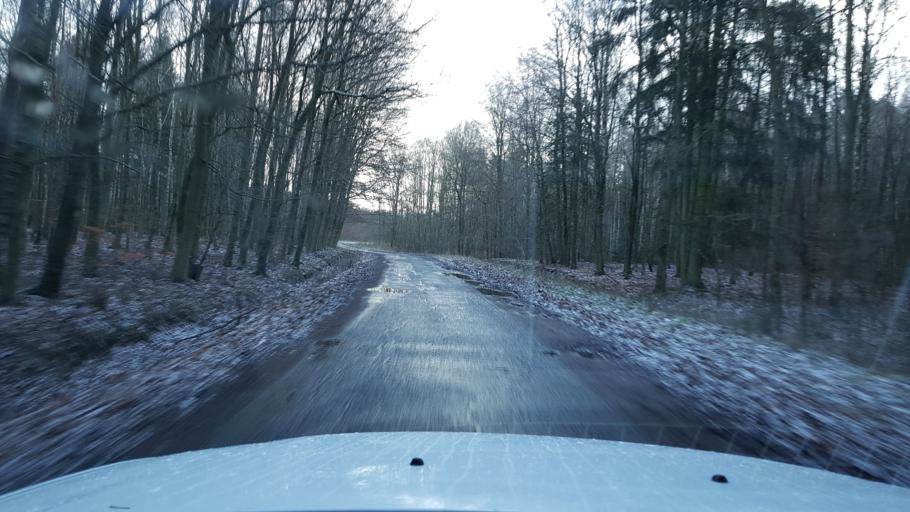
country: PL
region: West Pomeranian Voivodeship
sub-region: Powiat gryficki
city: Trzebiatow
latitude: 54.0431
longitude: 15.3319
